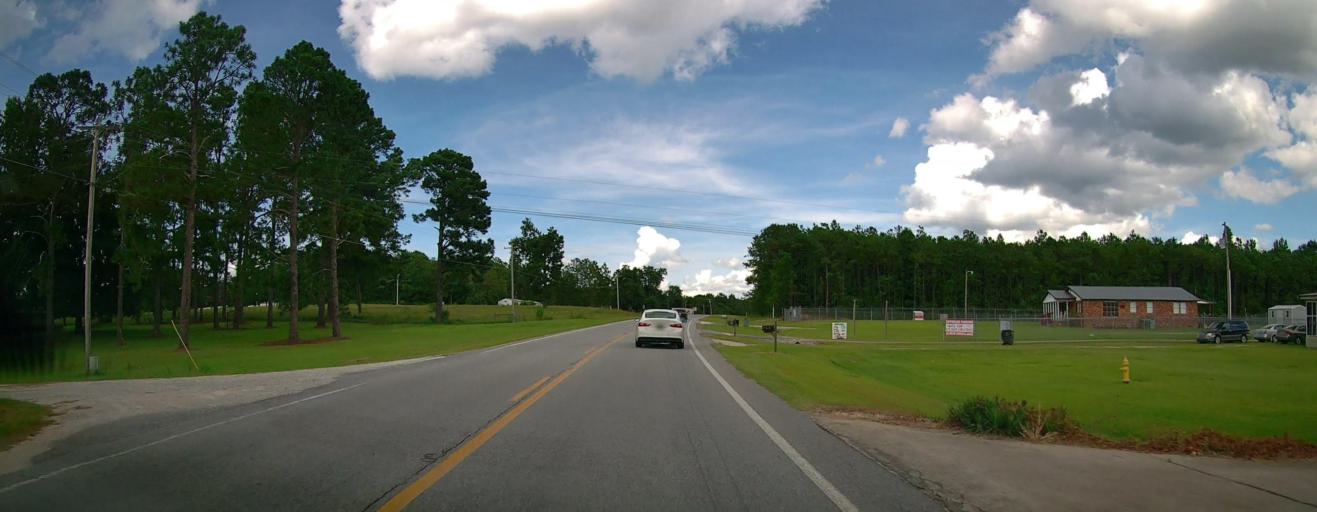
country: US
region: Alabama
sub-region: Russell County
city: Ladonia
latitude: 32.4502
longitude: -85.2336
